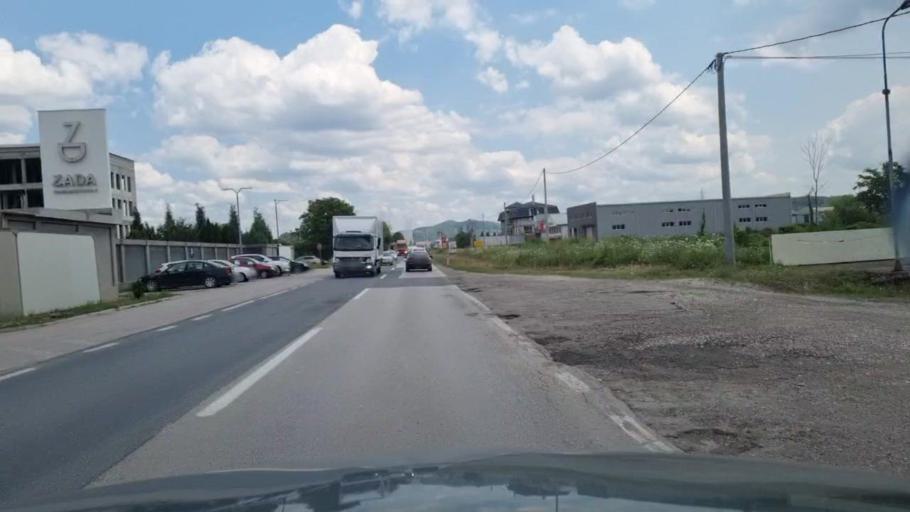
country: BA
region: Federation of Bosnia and Herzegovina
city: Kiseljak
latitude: 44.5139
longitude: 18.5697
